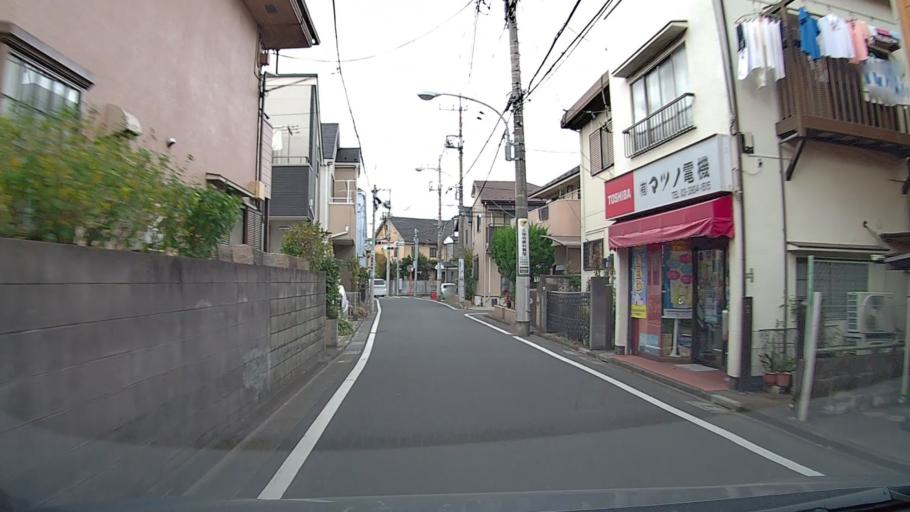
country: JP
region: Tokyo
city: Musashino
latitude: 35.7358
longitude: 139.6064
